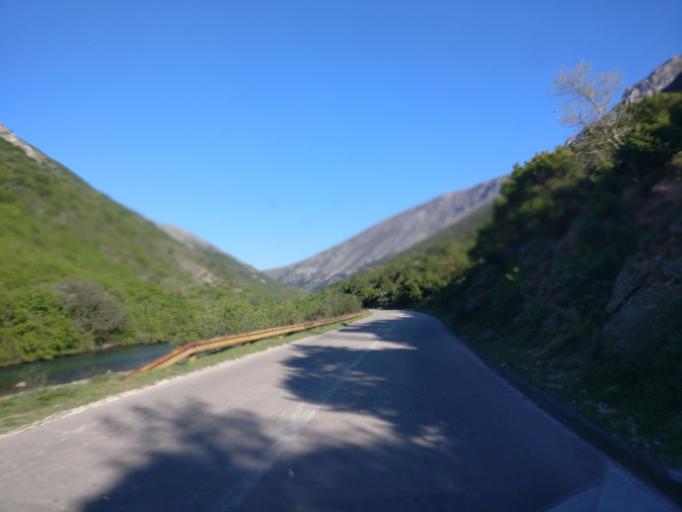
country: BA
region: Federation of Bosnia and Herzegovina
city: Stolac
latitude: 43.0805
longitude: 18.0128
